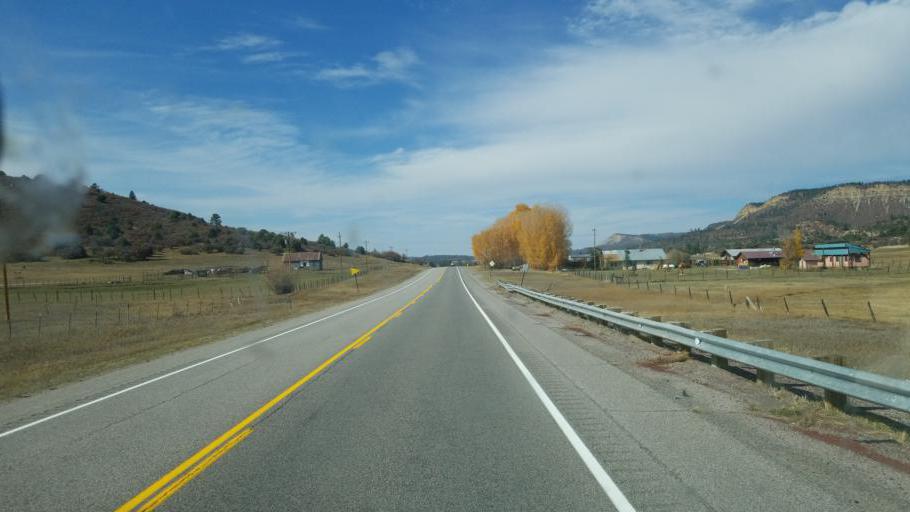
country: US
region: New Mexico
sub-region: Rio Arriba County
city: Chama
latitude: 36.8873
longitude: -106.6210
